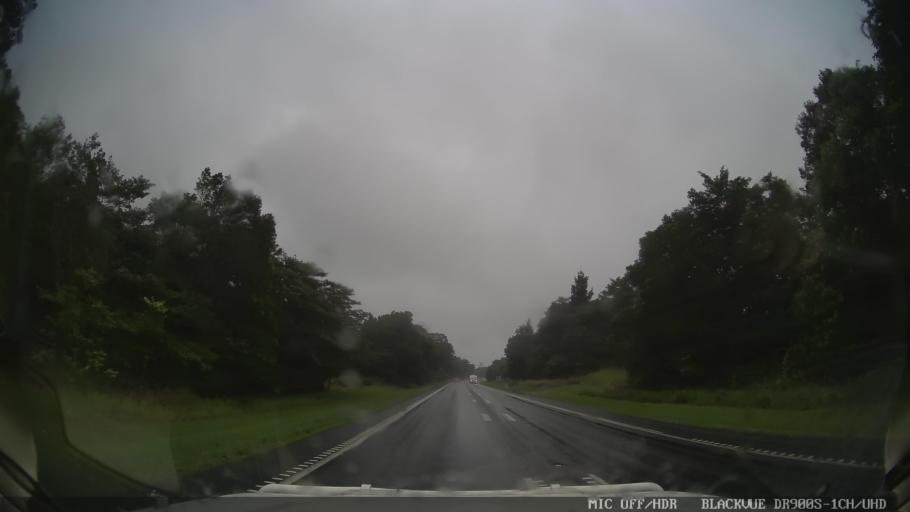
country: AU
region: Queensland
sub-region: Cassowary Coast
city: Innisfail
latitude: -17.8557
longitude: 145.9867
